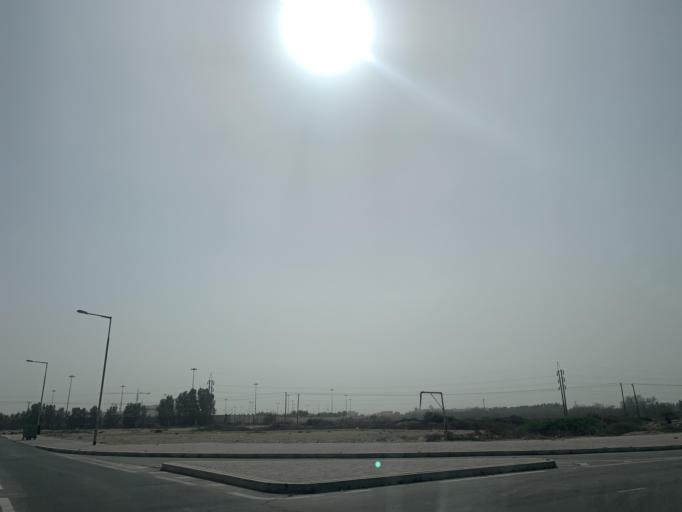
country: BH
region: Northern
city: Madinat `Isa
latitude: 26.1625
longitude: 50.5367
